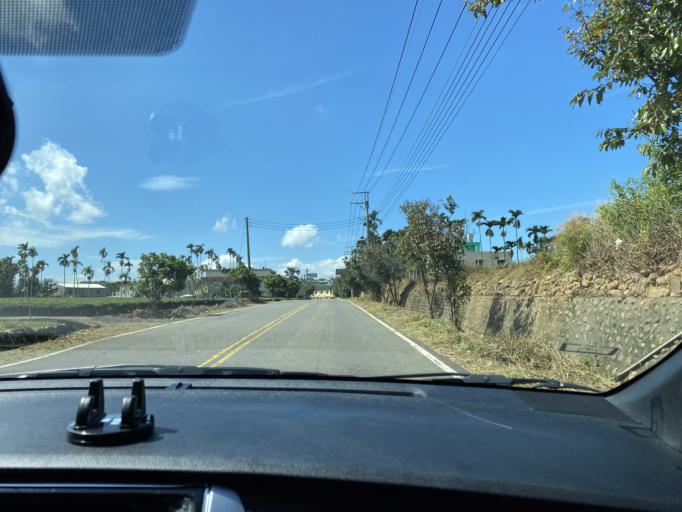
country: TW
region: Taiwan
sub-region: Nantou
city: Nantou
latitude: 23.8634
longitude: 120.6329
